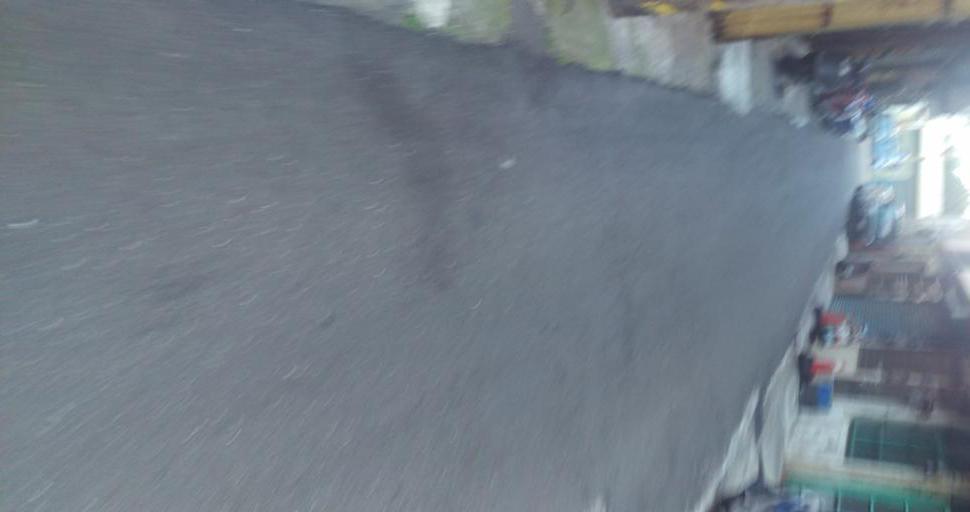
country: TW
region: Taiwan
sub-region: Hsinchu
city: Zhubei
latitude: 24.7438
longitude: 121.0850
